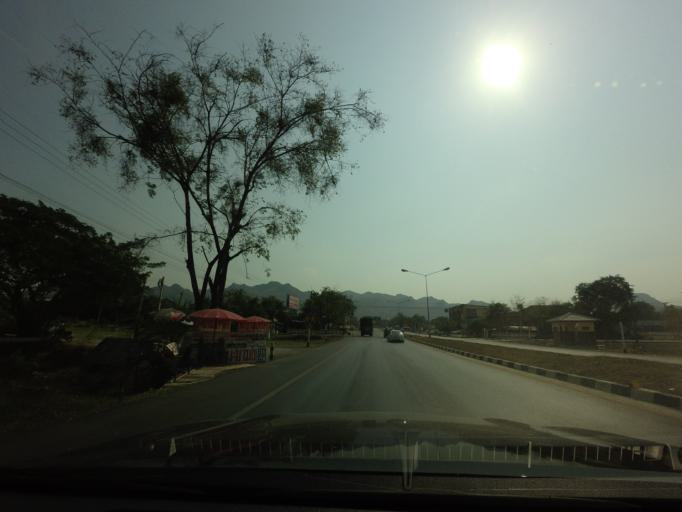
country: TH
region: Kanchanaburi
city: Kanchanaburi
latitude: 13.9931
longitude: 99.5691
